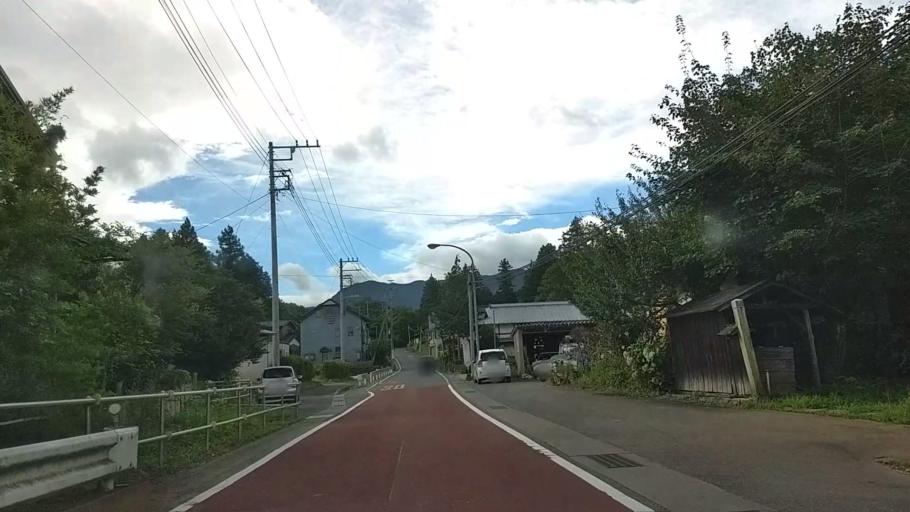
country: JP
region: Yamanashi
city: Uenohara
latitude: 35.5936
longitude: 139.1496
